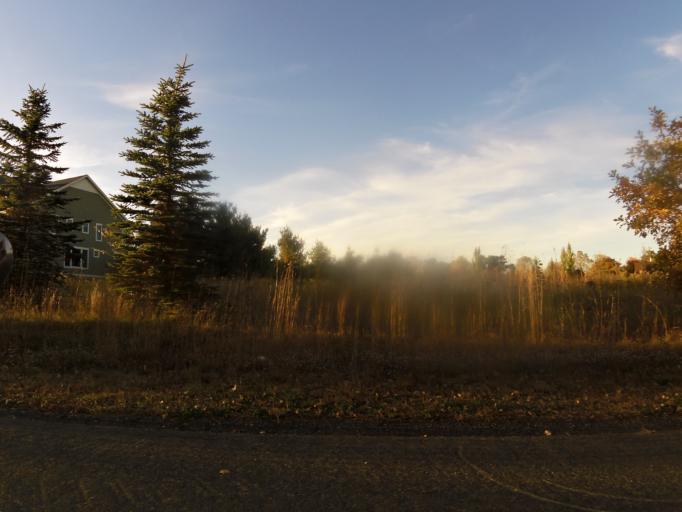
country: US
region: Minnesota
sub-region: Washington County
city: Lake Elmo
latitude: 44.9802
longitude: -92.8520
